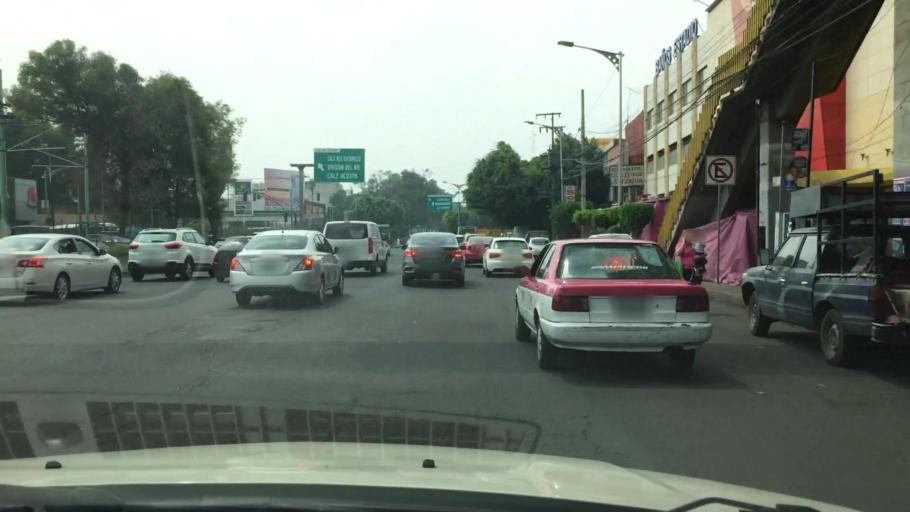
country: MX
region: Mexico City
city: Tlalpan
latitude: 19.2988
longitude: -99.1508
